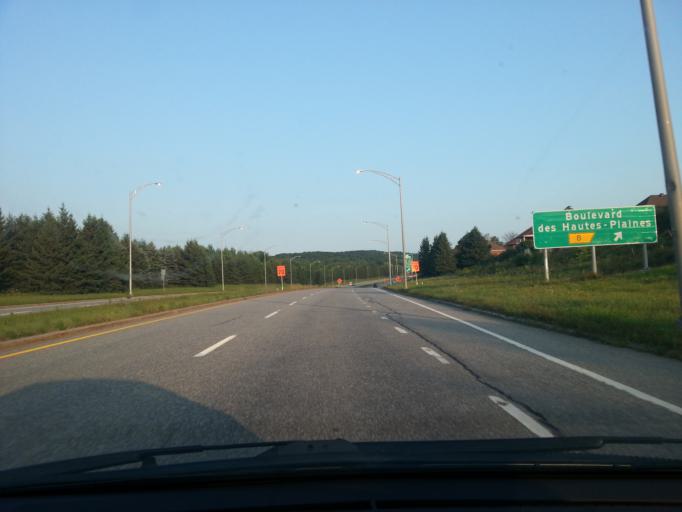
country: CA
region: Quebec
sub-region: Outaouais
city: Gatineau
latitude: 45.4715
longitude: -75.7679
